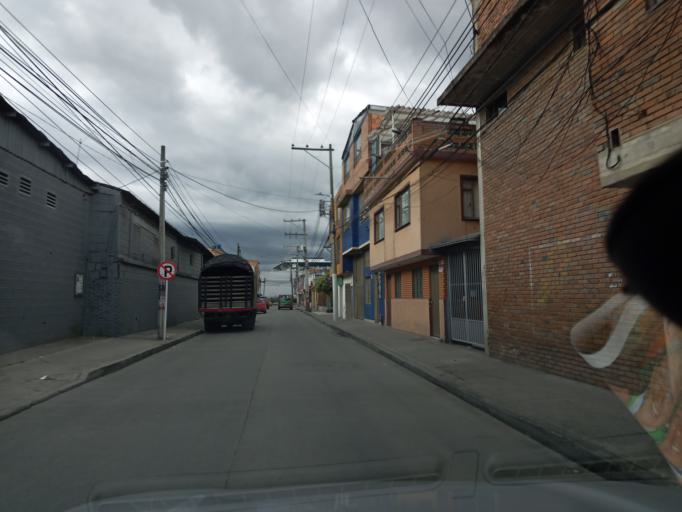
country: CO
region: Cundinamarca
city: Funza
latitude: 4.6870
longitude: -74.1308
